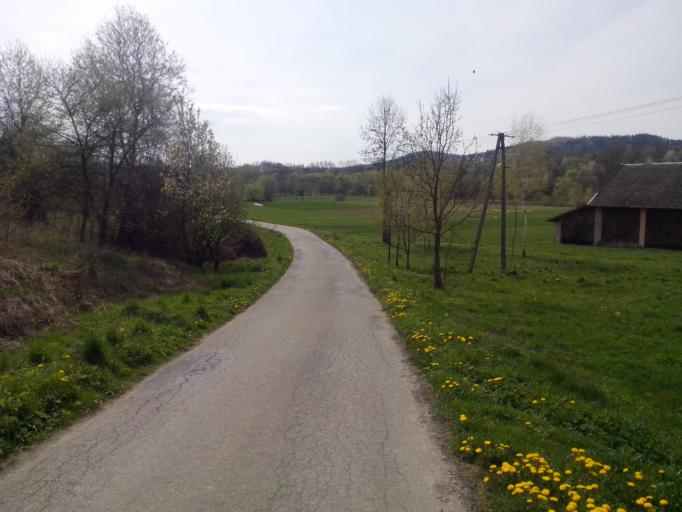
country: PL
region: Subcarpathian Voivodeship
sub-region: Powiat strzyzowski
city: Jawornik
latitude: 49.8242
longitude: 21.8369
